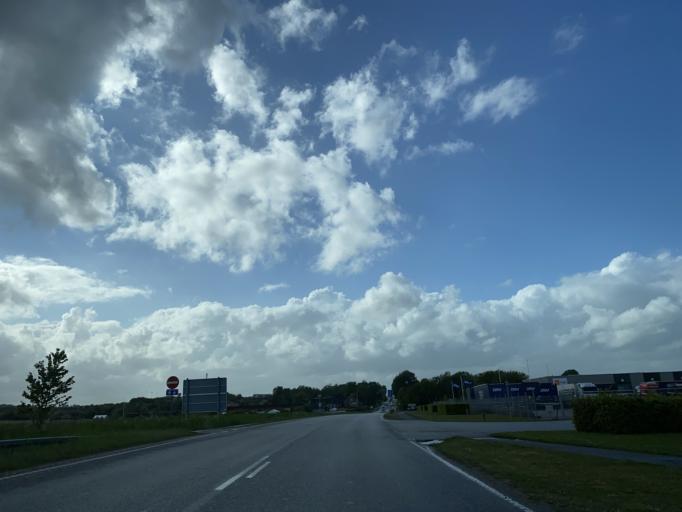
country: DK
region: Central Jutland
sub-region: Horsens Kommune
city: Horsens
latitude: 55.8895
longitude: 9.7768
